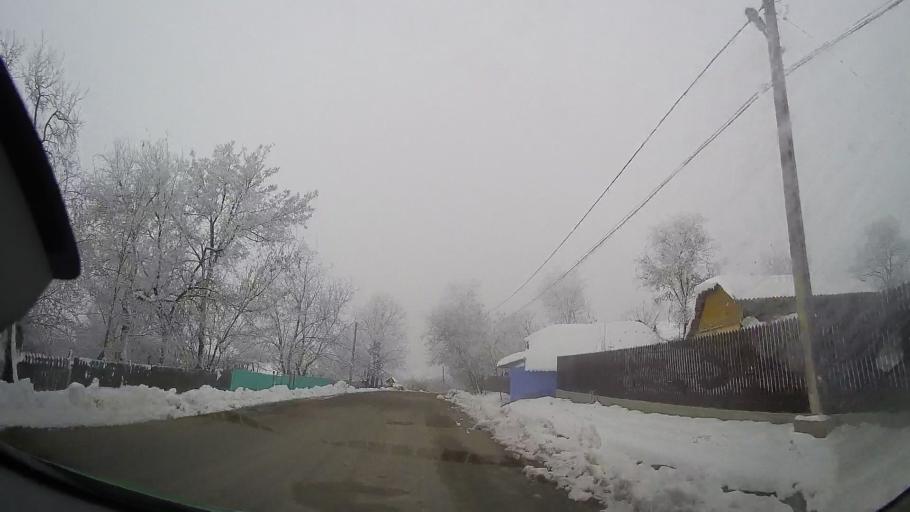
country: RO
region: Iasi
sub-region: Comuna Tansa
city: Suhulet
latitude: 46.8932
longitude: 27.2857
